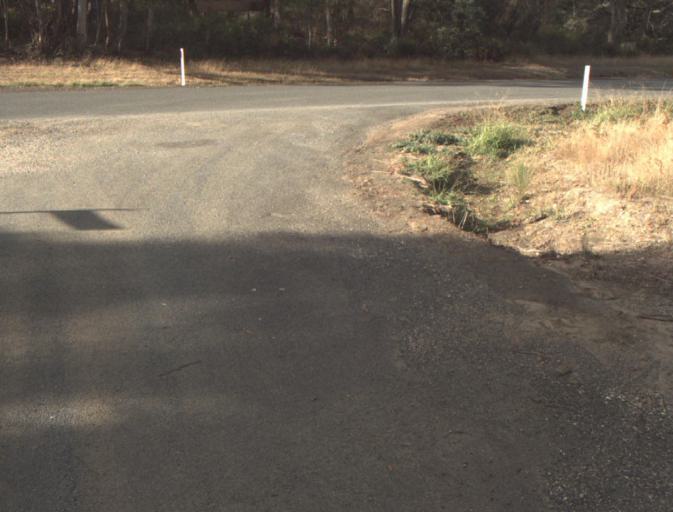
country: AU
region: Tasmania
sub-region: Launceston
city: Mayfield
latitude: -41.2399
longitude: 147.1952
